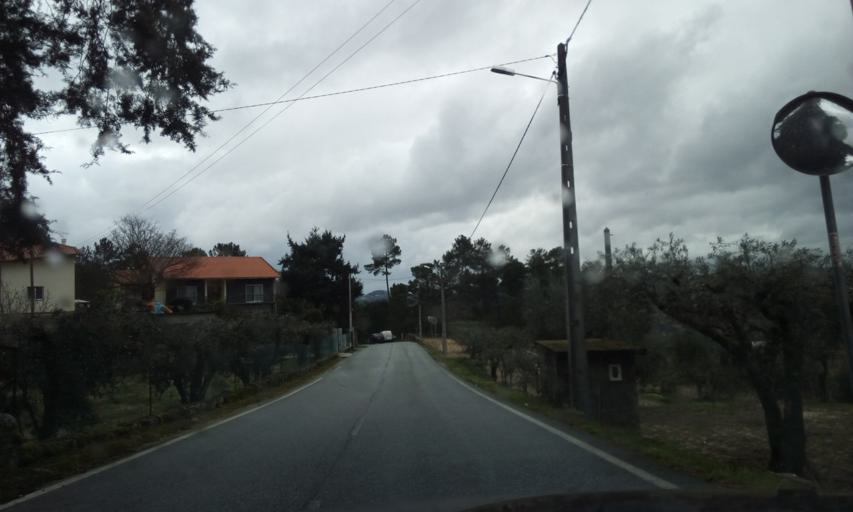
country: PT
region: Viseu
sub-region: Viseu
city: Rio de Loba
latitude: 40.6038
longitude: -7.8463
